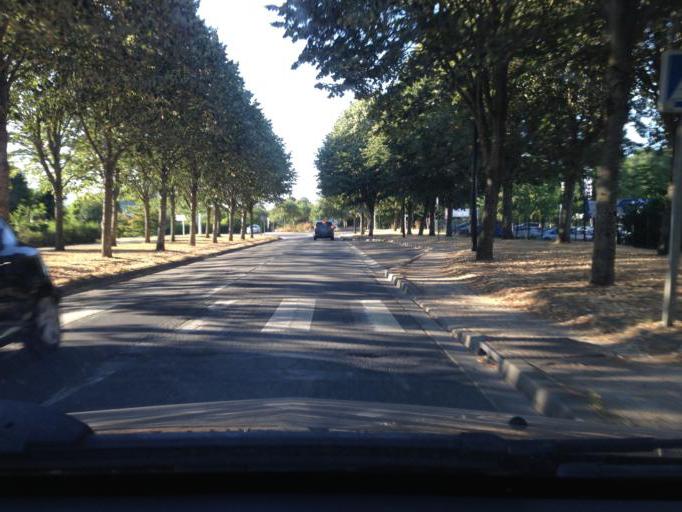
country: FR
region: Ile-de-France
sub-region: Departement des Yvelines
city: Chateaufort
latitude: 48.7277
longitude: 2.0818
